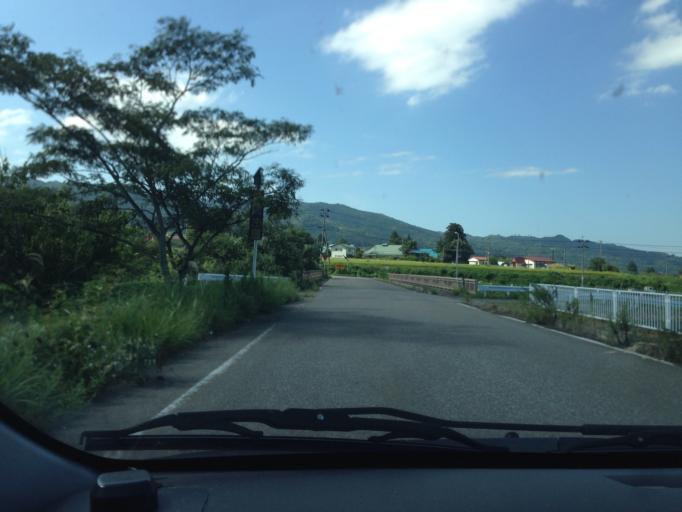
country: JP
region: Fukushima
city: Kitakata
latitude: 37.4347
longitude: 139.8168
